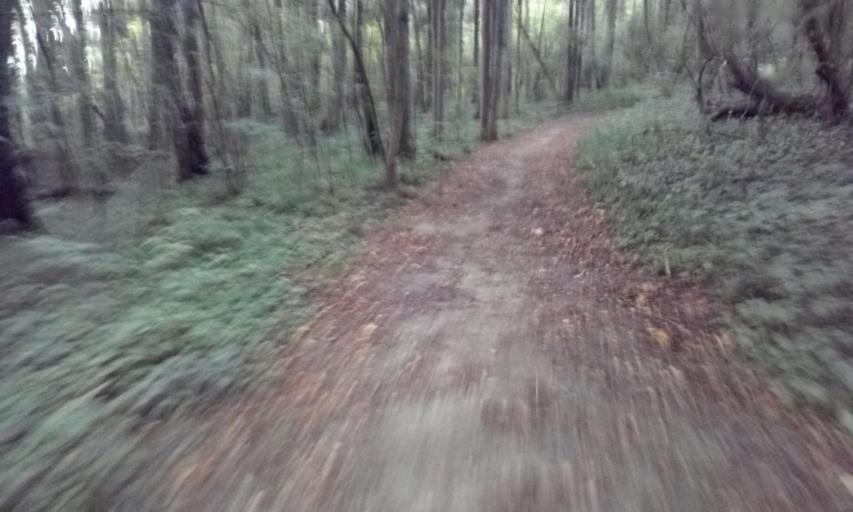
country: RU
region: Moskovskaya
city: Moskovskiy
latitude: 55.5943
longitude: 37.3295
